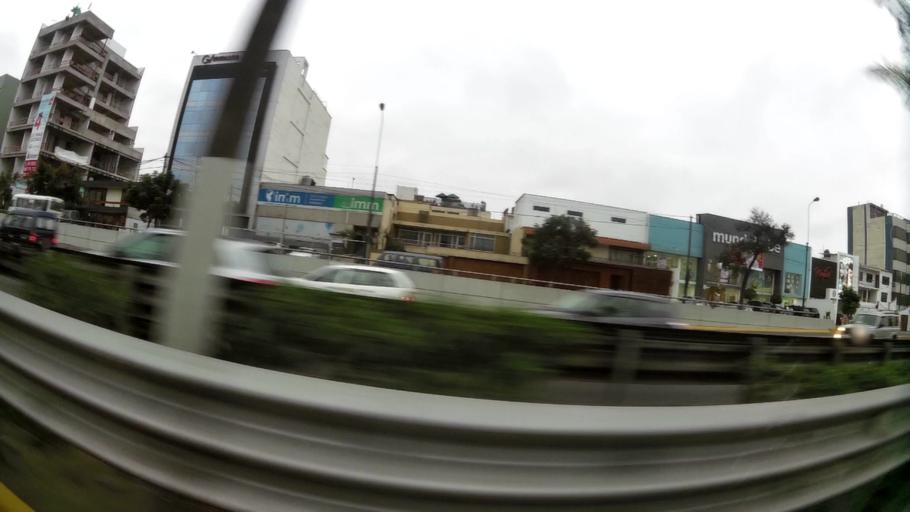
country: PE
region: Lima
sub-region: Lima
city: San Luis
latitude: -12.0893
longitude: -77.0119
